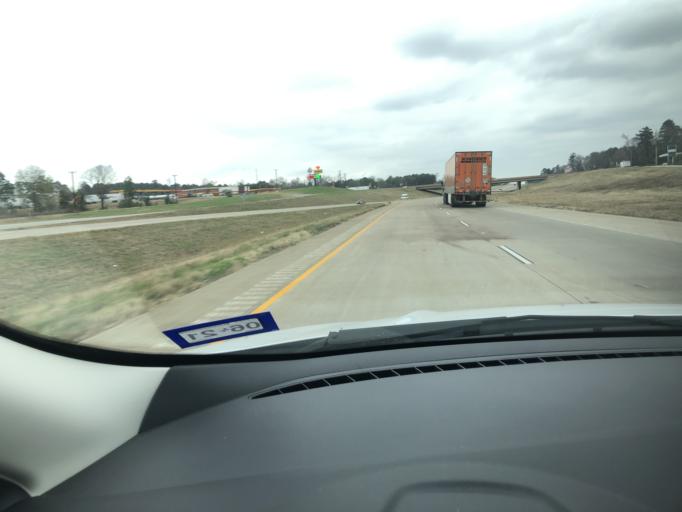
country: US
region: Texas
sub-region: Angelina County
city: Redland
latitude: 31.4139
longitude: -94.7213
